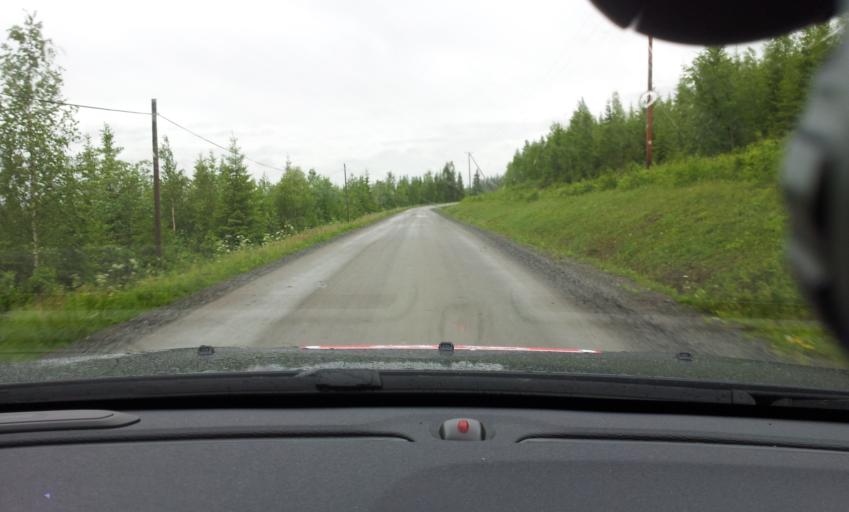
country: SE
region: Jaemtland
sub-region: Are Kommun
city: Are
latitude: 63.4126
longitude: 12.8279
